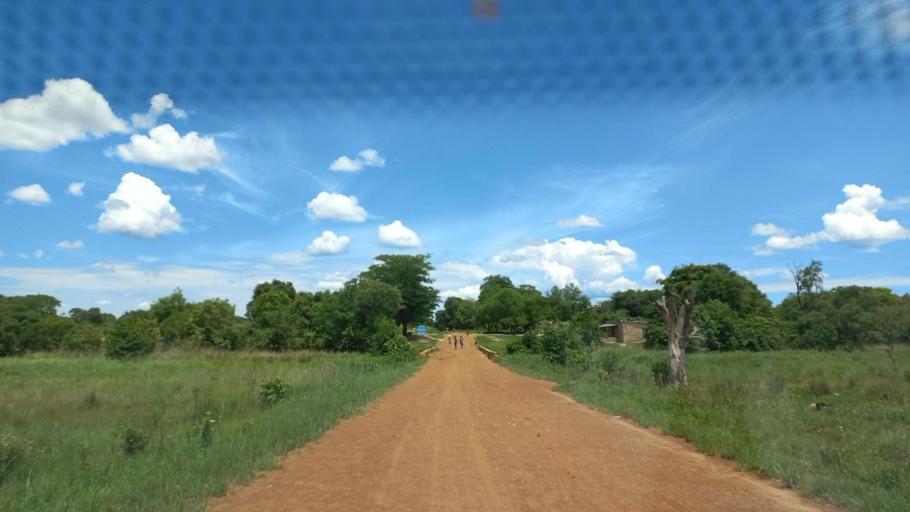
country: ZM
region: North-Western
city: Kabompo
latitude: -12.7478
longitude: 24.2670
